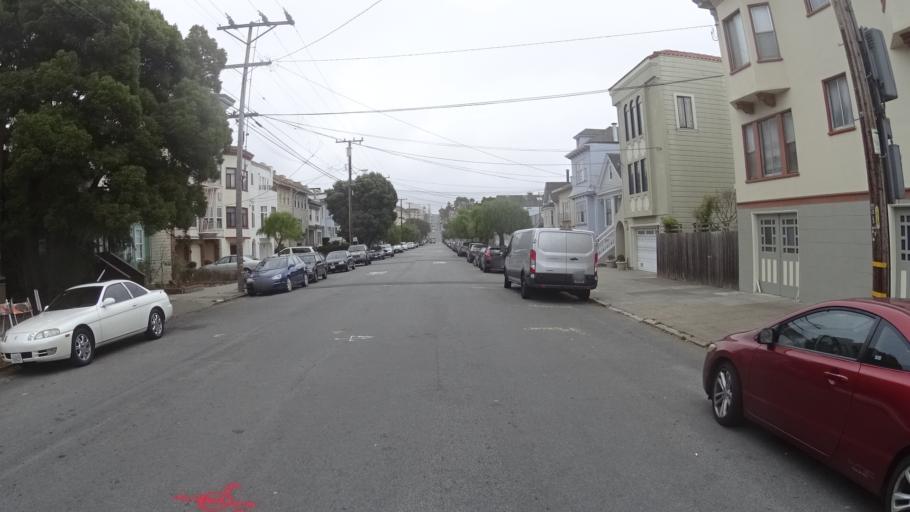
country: US
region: California
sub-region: San Francisco County
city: San Francisco
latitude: 37.7835
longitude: -122.4904
